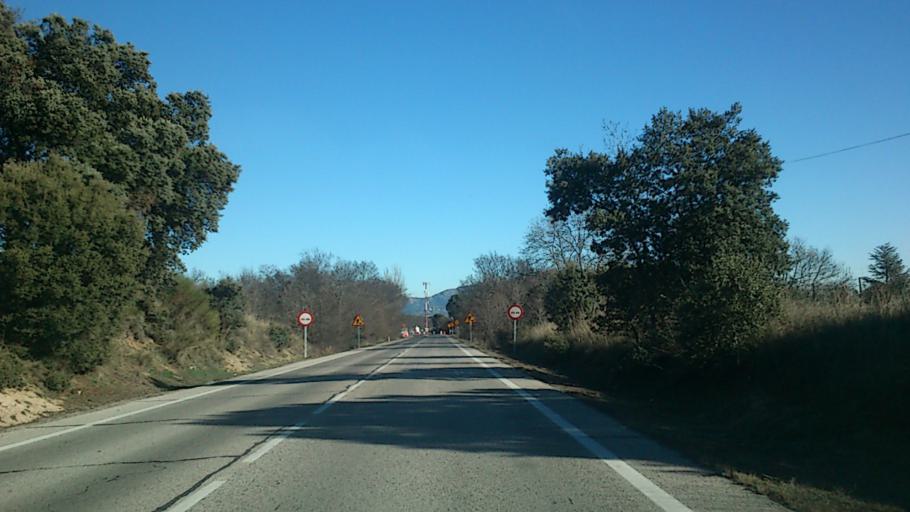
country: ES
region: Madrid
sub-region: Provincia de Madrid
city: Guadarrama
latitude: 40.6516
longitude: -4.0729
